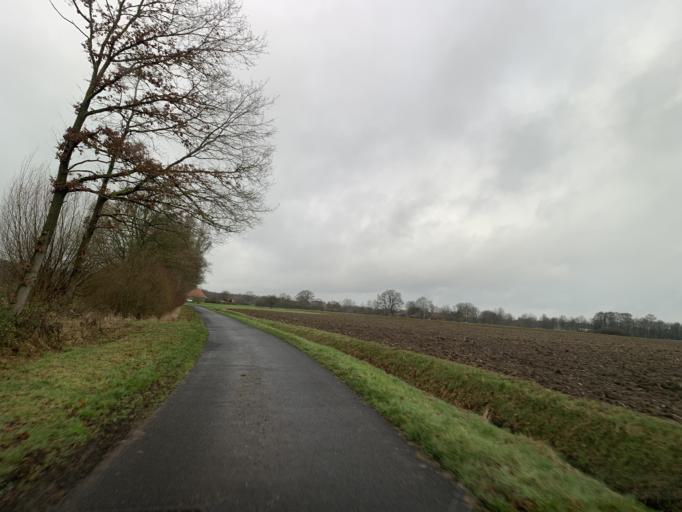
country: DE
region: North Rhine-Westphalia
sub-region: Regierungsbezirk Munster
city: Senden
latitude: 51.9009
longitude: 7.5223
